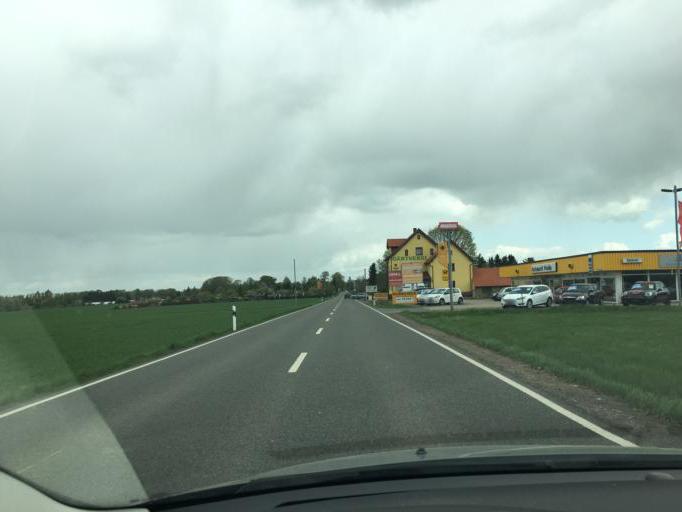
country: DE
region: Saxony
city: Limbach-Oberfrohna
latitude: 50.8407
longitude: 12.7677
